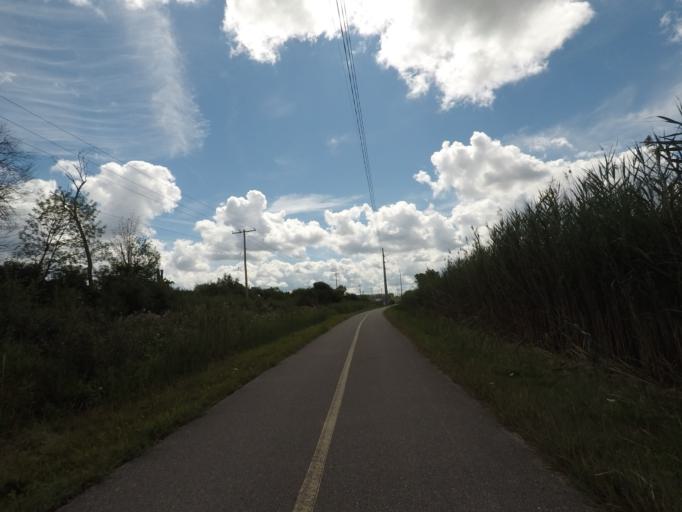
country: US
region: Wisconsin
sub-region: Waukesha County
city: Pewaukee
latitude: 43.0489
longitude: -88.2741
